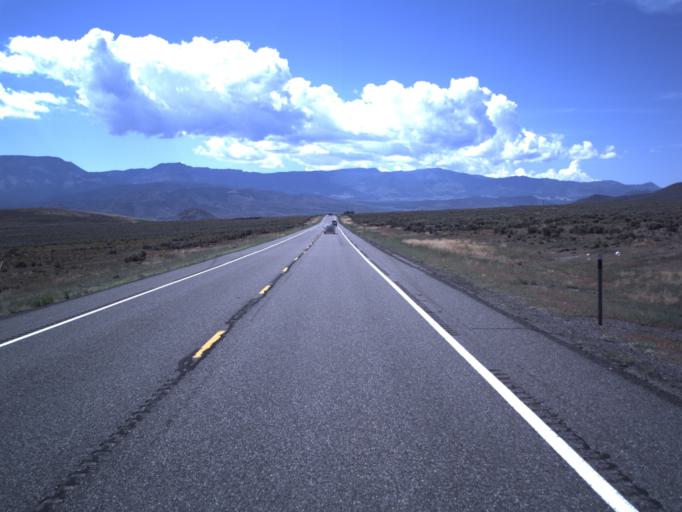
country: US
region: Utah
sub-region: Piute County
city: Junction
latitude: 38.2727
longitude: -112.2230
